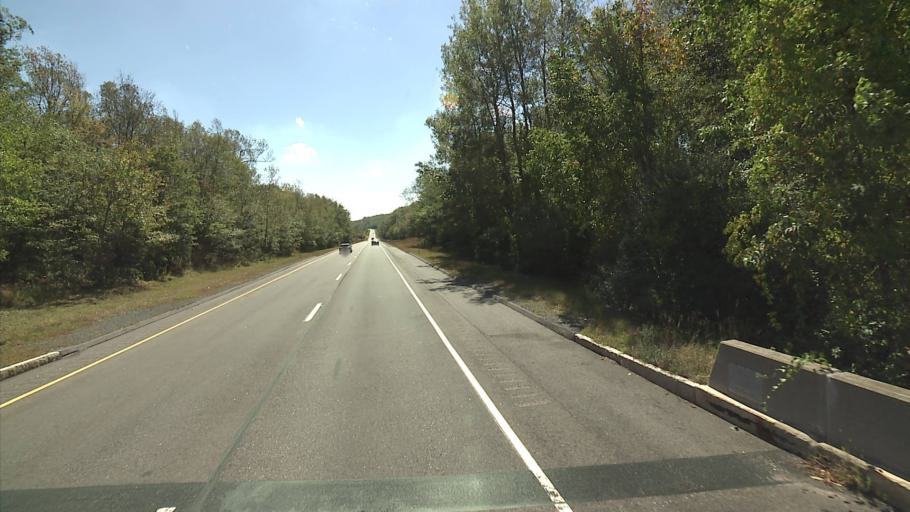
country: US
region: Connecticut
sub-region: New London County
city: Colchester
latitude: 41.5013
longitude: -72.3024
